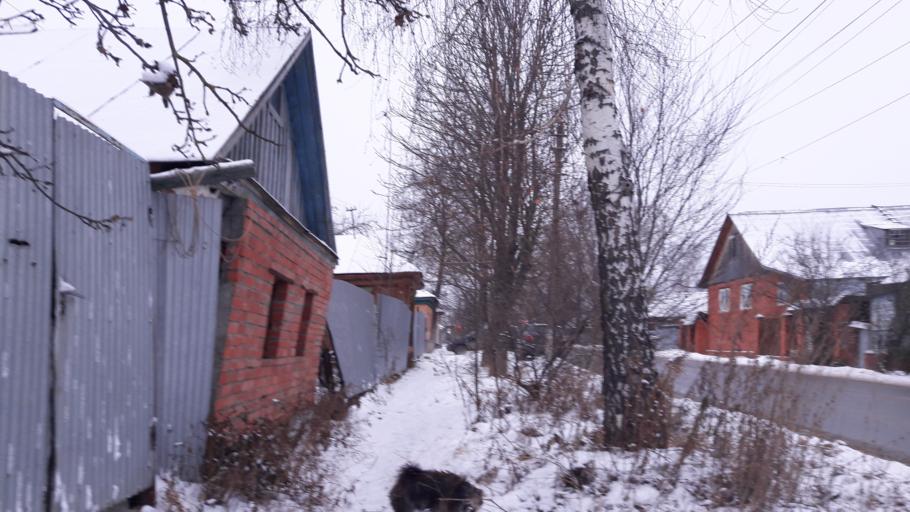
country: RU
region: Tula
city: Gorelki
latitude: 54.2391
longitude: 37.6327
